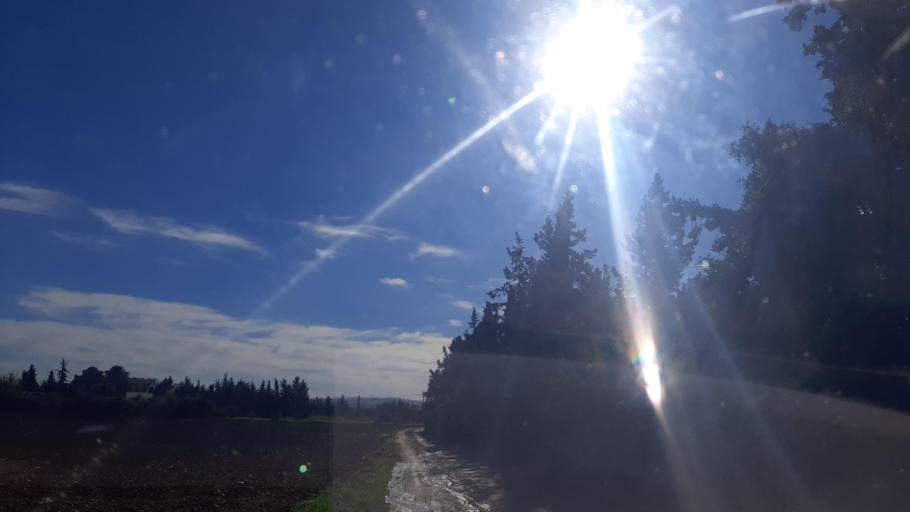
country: TN
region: Tunis
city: Oued Lill
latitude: 36.7598
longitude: 9.9819
